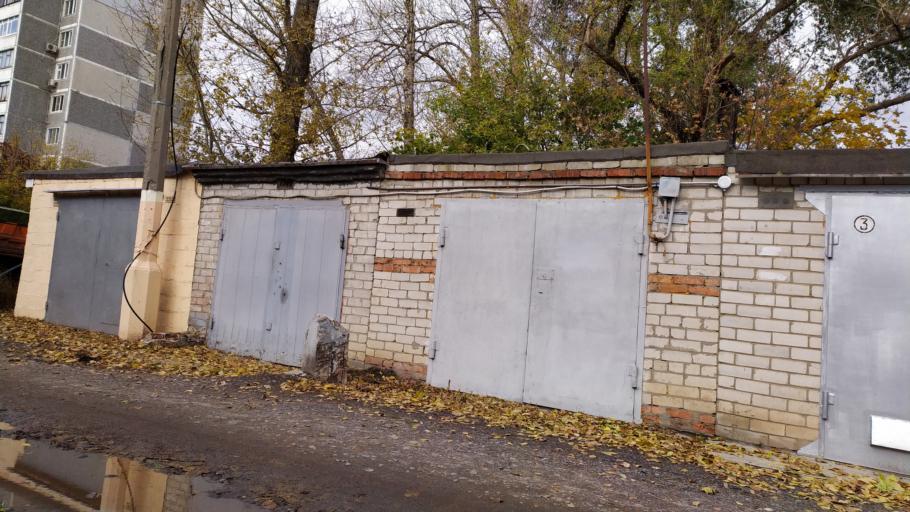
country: RU
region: Kursk
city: Kursk
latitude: 51.6505
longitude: 36.1474
